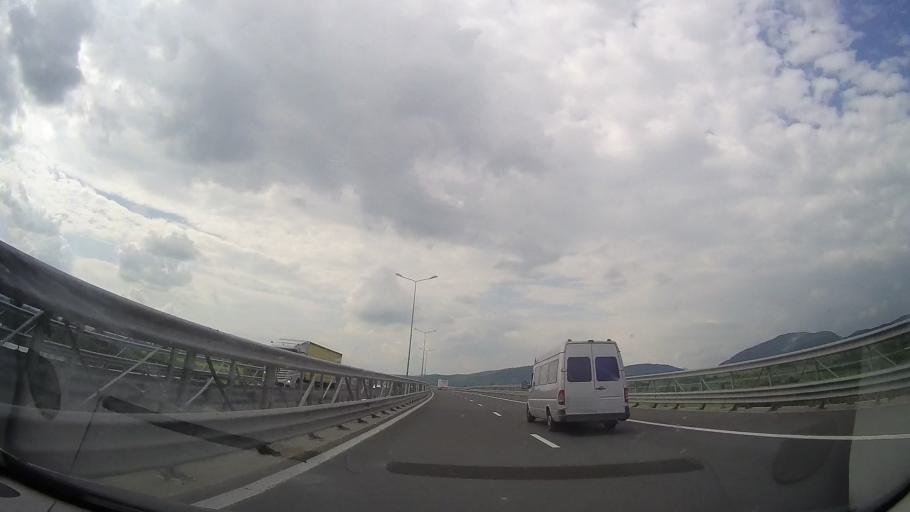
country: RO
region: Hunedoara
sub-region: Oras Simeria
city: Simeria
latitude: 45.8672
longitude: 23.0223
